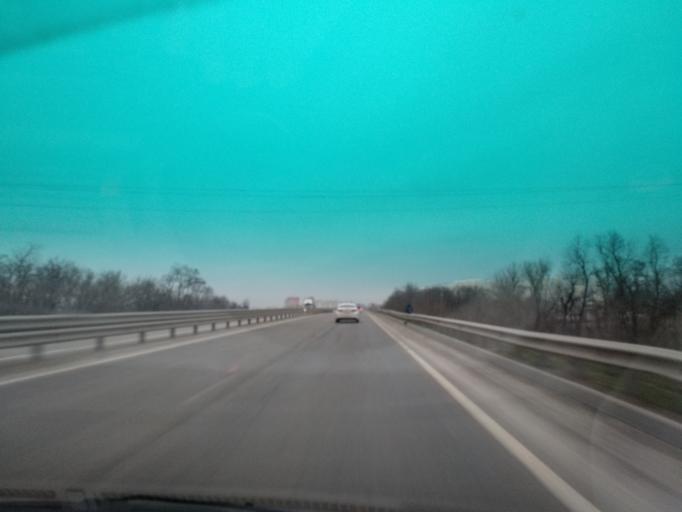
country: RU
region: Krasnodarskiy
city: Pashkovskiy
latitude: 45.0464
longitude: 39.1292
